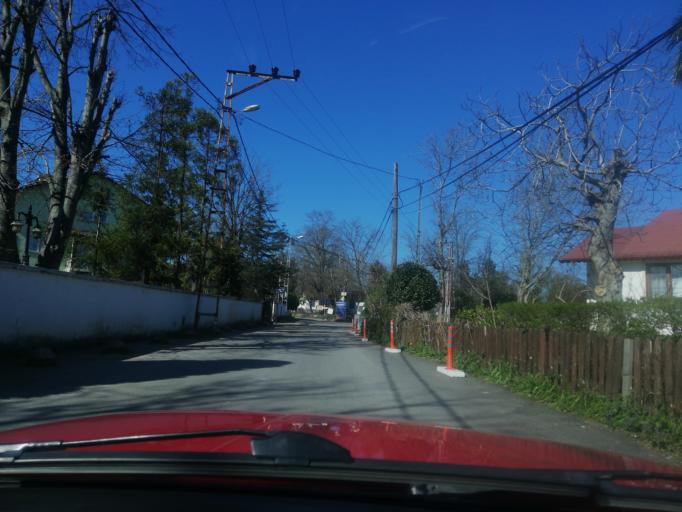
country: TR
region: Istanbul
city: Mahmut Sevket Pasa
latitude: 41.1135
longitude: 29.2116
